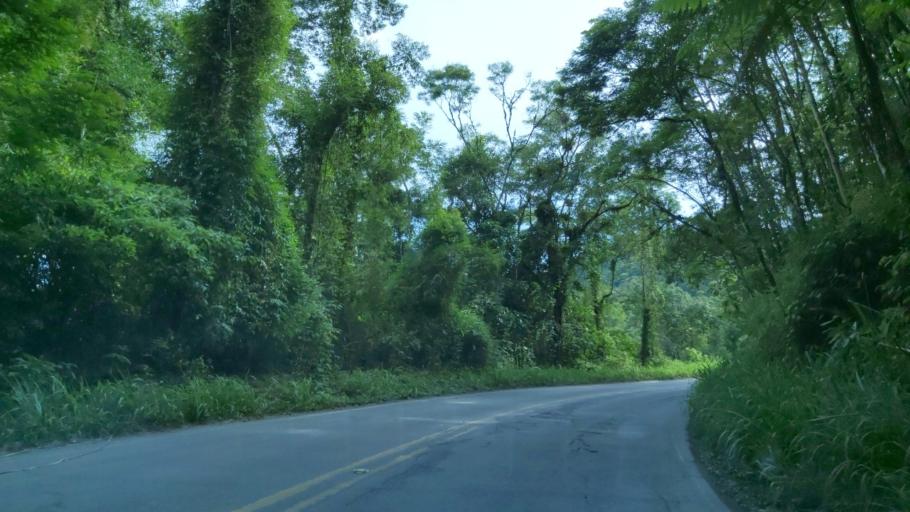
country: BR
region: Sao Paulo
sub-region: Miracatu
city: Miracatu
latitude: -24.0542
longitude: -47.5738
